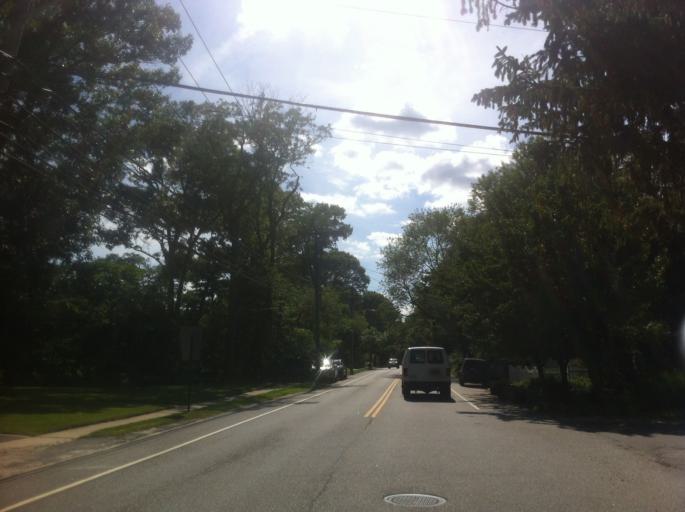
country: US
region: New York
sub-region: Nassau County
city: Syosset
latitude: 40.8259
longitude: -73.5049
